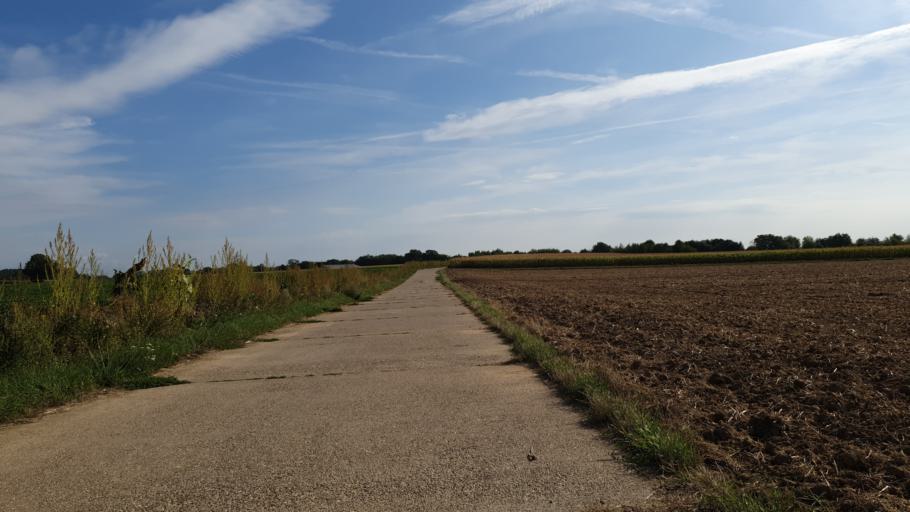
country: DE
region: Rheinland-Pfalz
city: Winden
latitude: 49.1152
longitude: 8.1215
